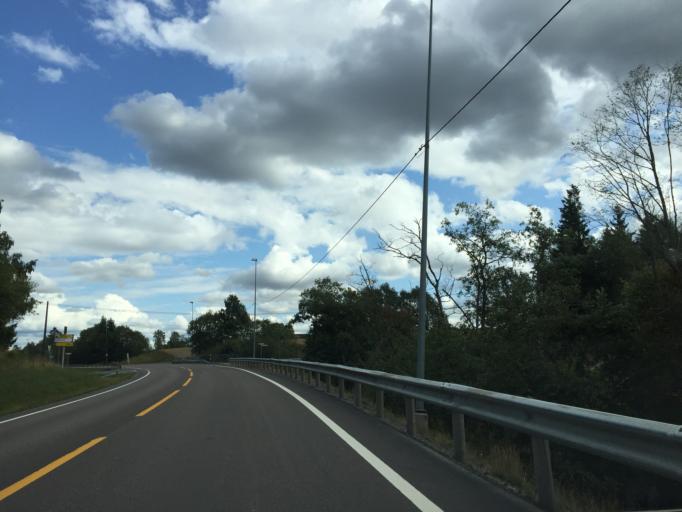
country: NO
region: Ostfold
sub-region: Hobol
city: Elvestad
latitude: 59.6226
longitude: 10.9817
